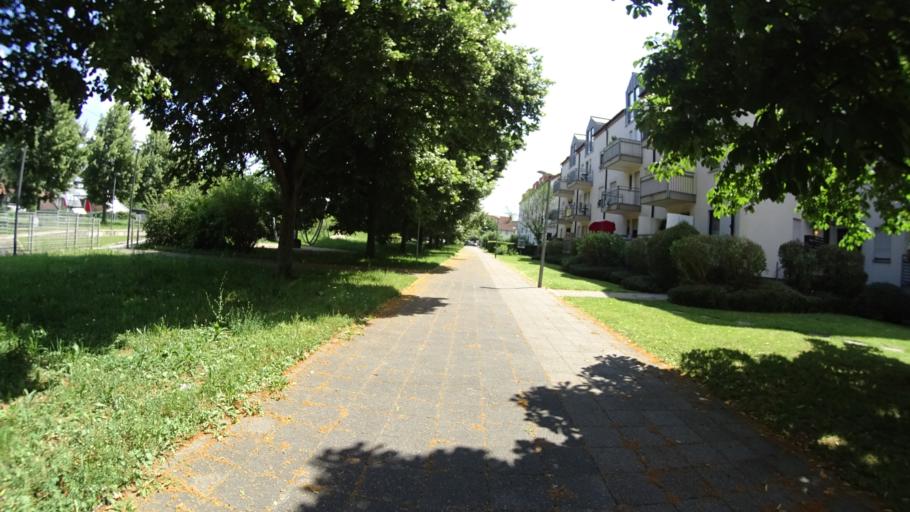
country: DE
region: Baden-Wuerttemberg
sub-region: Karlsruhe Region
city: Karlsruhe
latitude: 48.9893
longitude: 8.4519
